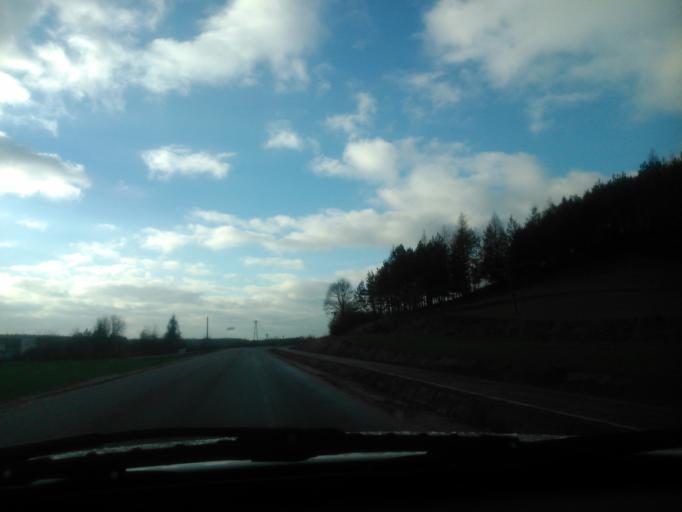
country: PL
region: Kujawsko-Pomorskie
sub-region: Powiat golubsko-dobrzynski
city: Golub-Dobrzyn
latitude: 53.1292
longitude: 19.0870
